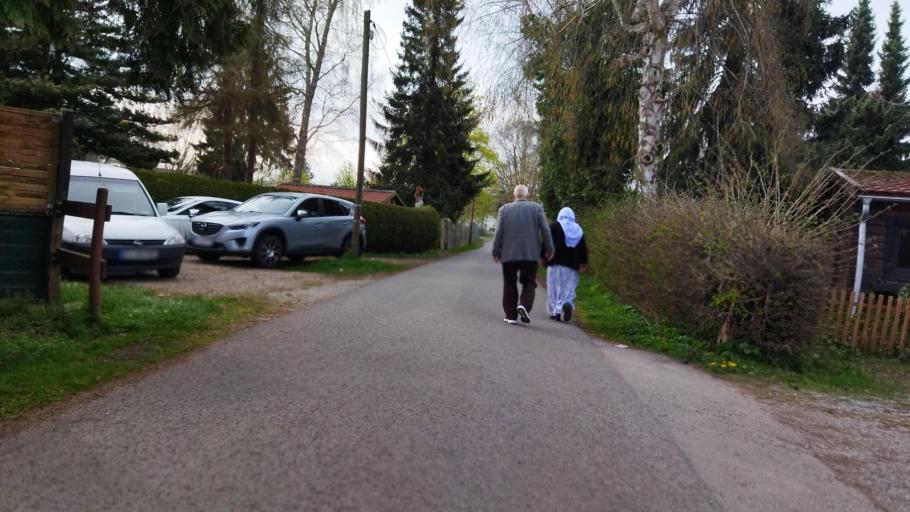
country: DE
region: Lower Saxony
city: Rinteln
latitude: 52.1927
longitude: 9.0859
